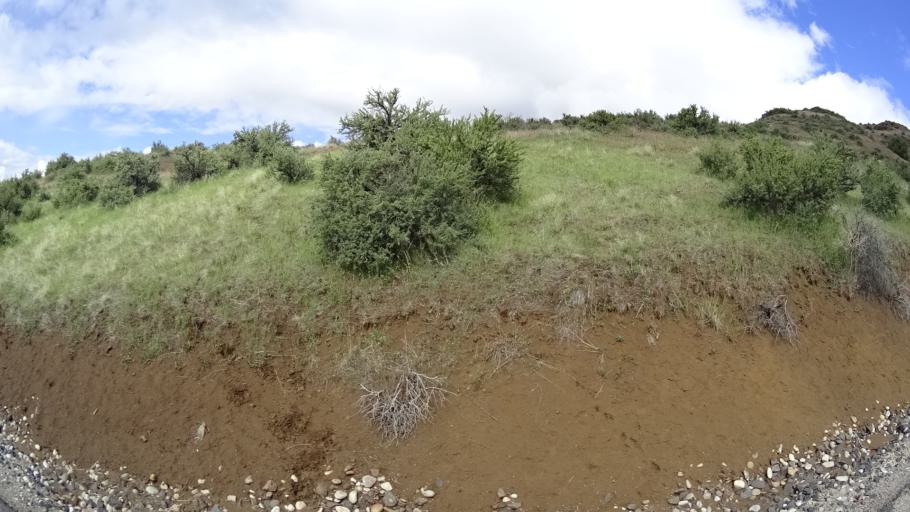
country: US
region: Idaho
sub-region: Ada County
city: Garden City
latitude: 43.7322
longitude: -116.2300
